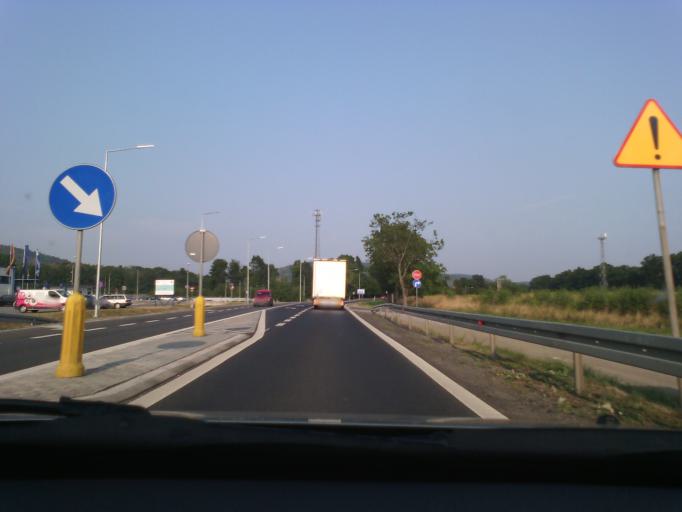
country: PL
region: Lower Silesian Voivodeship
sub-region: Powiat jeleniogorski
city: Janowice Wielkie
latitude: 50.9006
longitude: 15.8779
